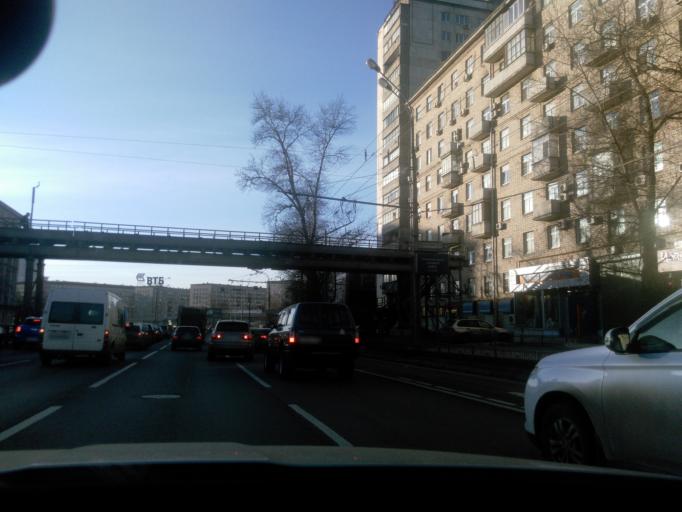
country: RU
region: Moskovskaya
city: Koptevo
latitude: 55.8093
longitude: 37.5056
